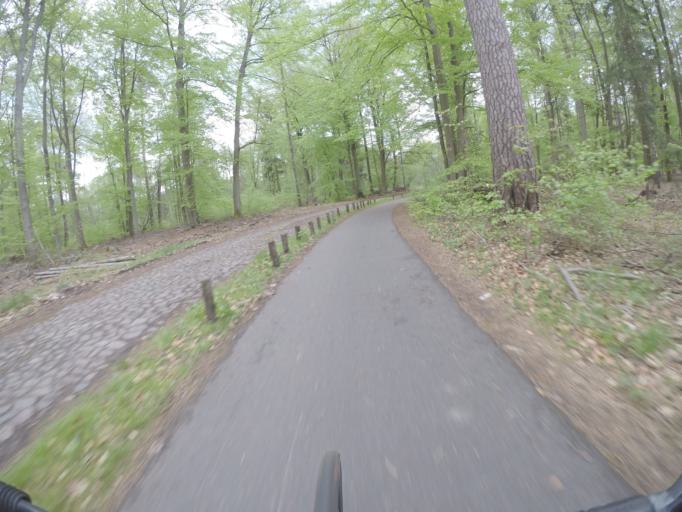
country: DE
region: Brandenburg
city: Marienwerder
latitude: 52.8288
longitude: 13.6472
